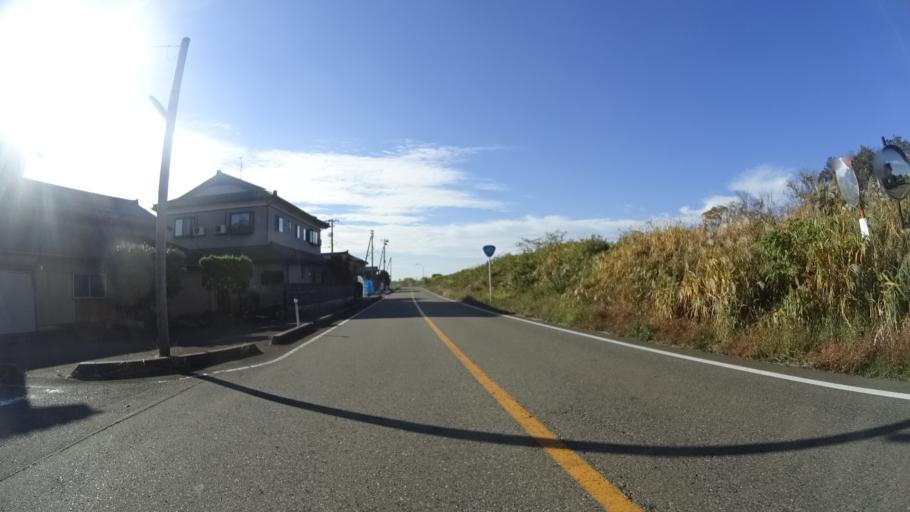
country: JP
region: Niigata
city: Yoshida-kasugacho
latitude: 37.5892
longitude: 138.8365
